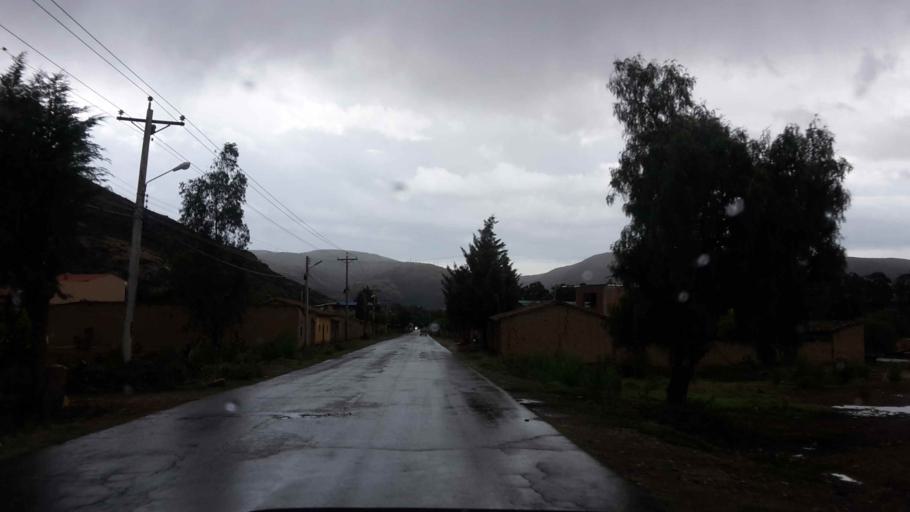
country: BO
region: Cochabamba
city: Tarata
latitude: -17.5476
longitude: -66.0998
